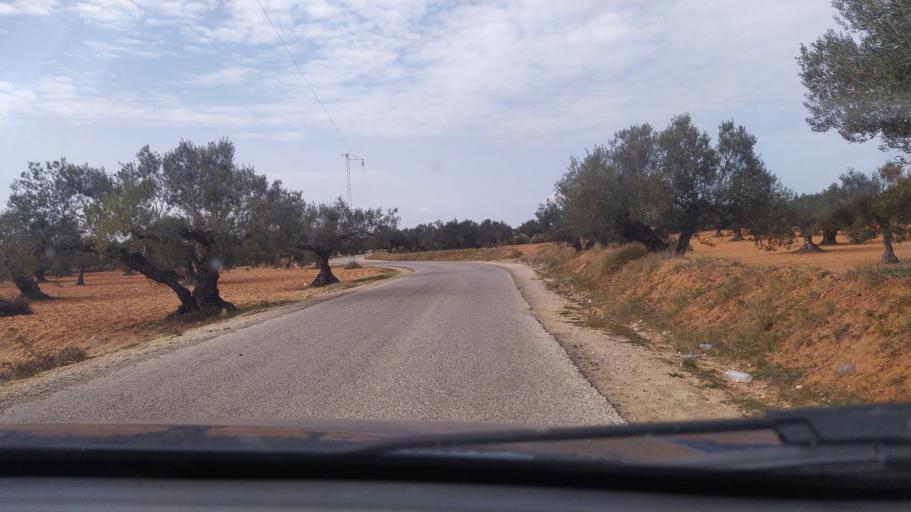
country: TN
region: Al Munastir
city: Sidi Bin Nur
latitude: 35.5255
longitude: 10.9686
